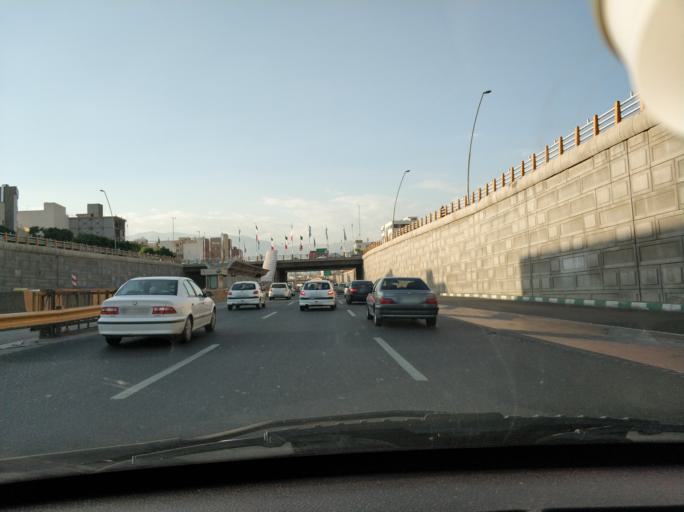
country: IR
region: Tehran
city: Tehran
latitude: 35.6957
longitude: 51.4568
